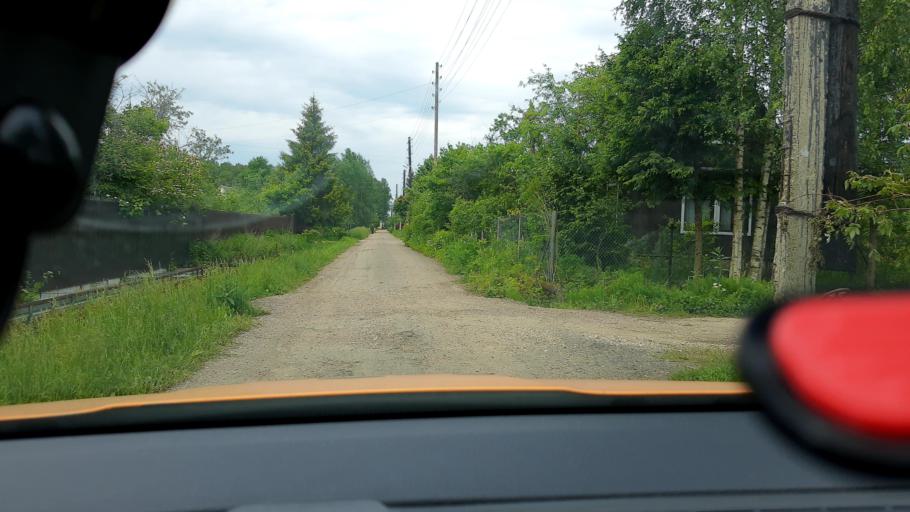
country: RU
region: Moskovskaya
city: Chupryakovo
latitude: 55.5633
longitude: 36.6596
